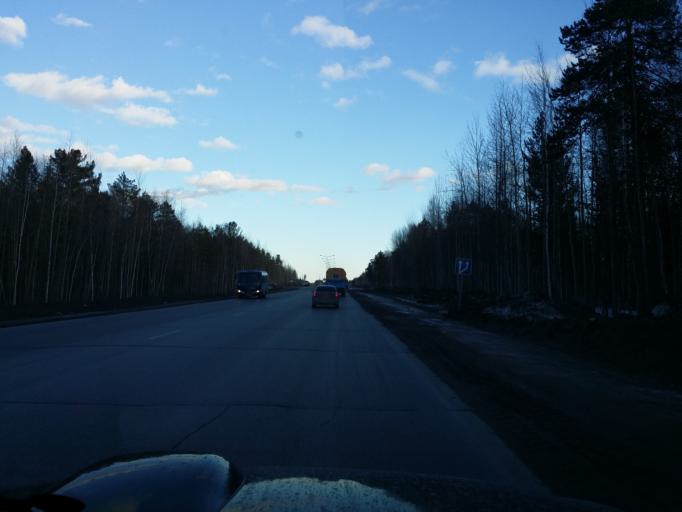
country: RU
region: Khanty-Mansiyskiy Avtonomnyy Okrug
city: Nizhnevartovsk
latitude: 61.0124
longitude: 76.3983
